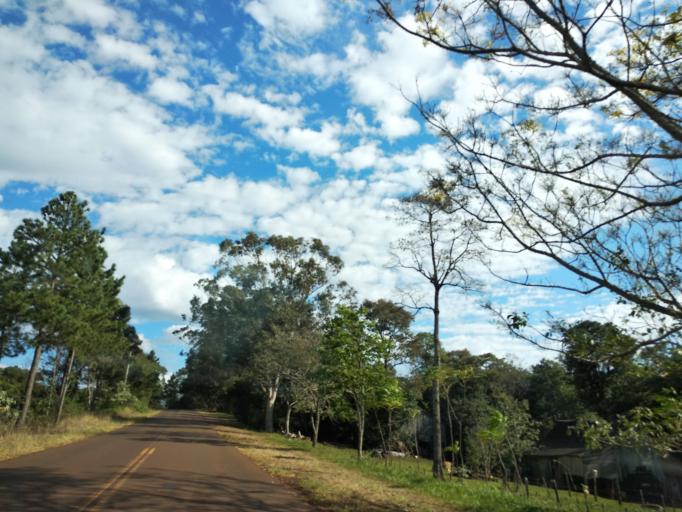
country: AR
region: Misiones
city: Aristobulo del Valle
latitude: -27.0723
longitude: -54.8309
